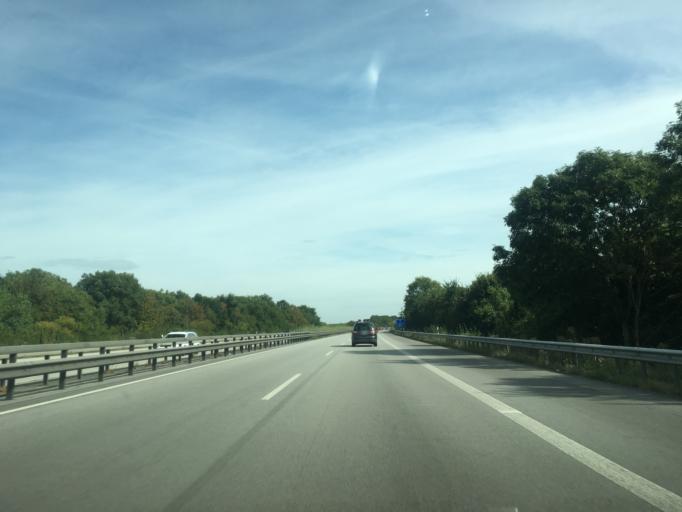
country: DE
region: Rheinland-Pfalz
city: Bermersheim
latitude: 49.6979
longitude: 8.2196
